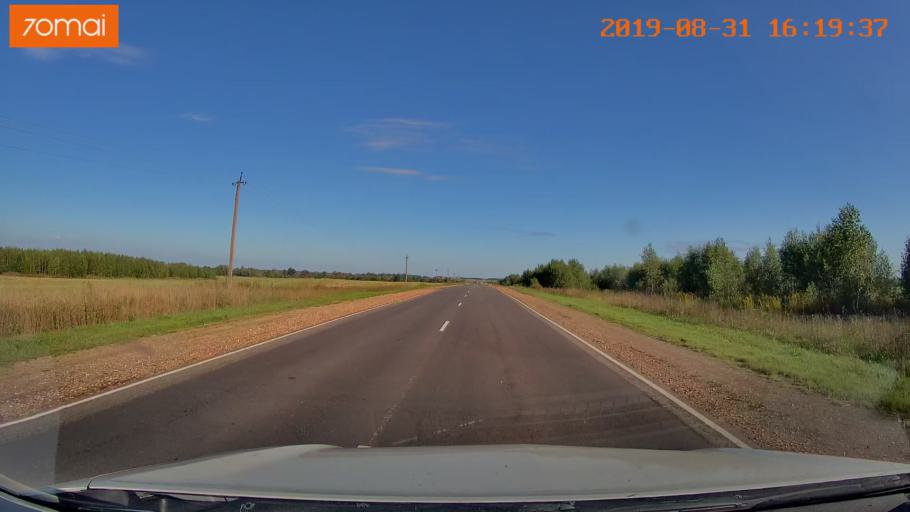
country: RU
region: Kaluga
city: Nikola-Lenivets
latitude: 54.5280
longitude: 35.5829
